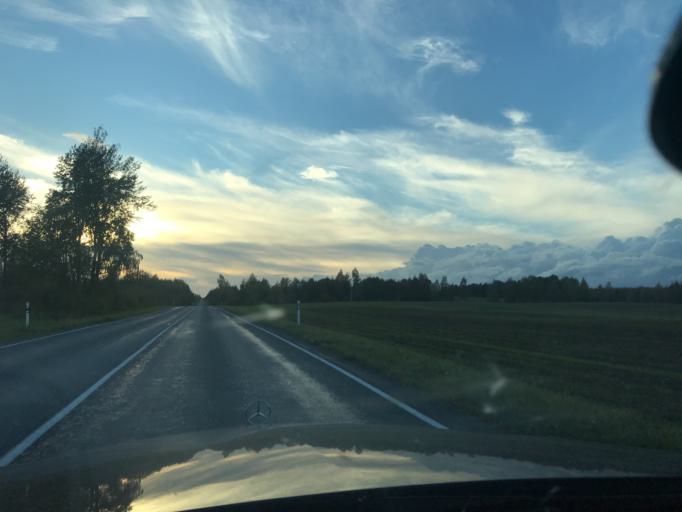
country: EE
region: Vorumaa
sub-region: Antsla vald
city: Vana-Antsla
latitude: 57.8784
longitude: 26.6742
